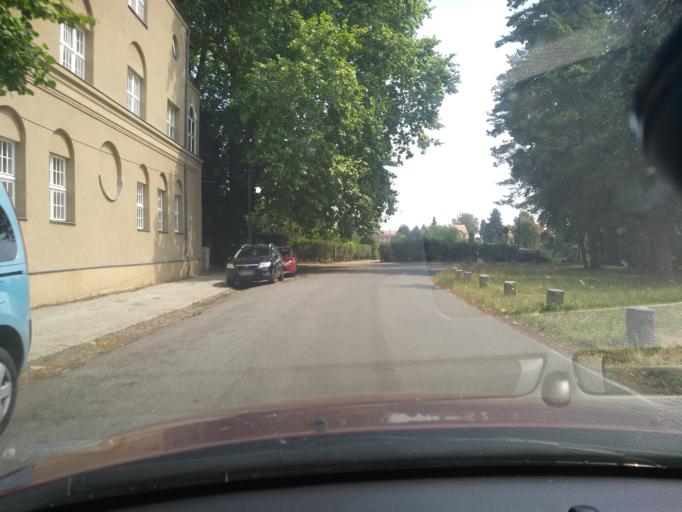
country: DE
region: Saxony
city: Goerlitz
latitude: 51.1402
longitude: 14.9718
